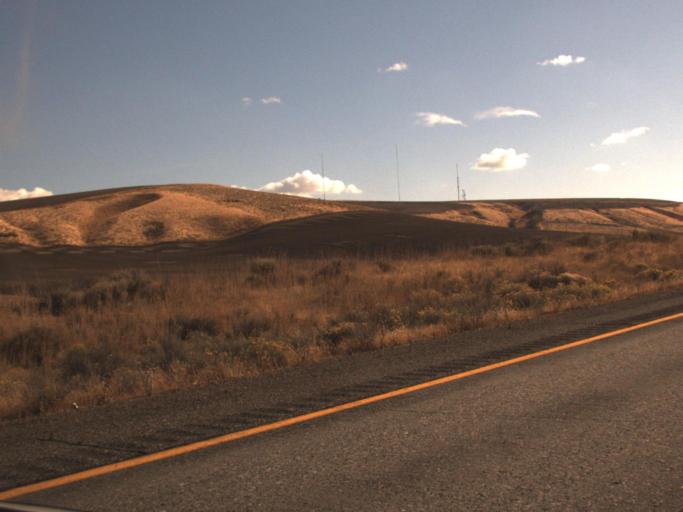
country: US
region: Washington
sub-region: Benton County
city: Highland
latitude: 46.1166
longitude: -119.2035
